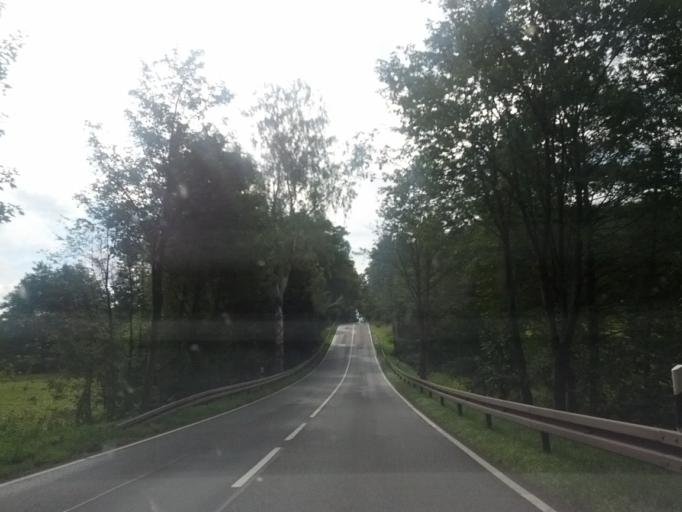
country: DE
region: Thuringia
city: Wolfsburg-Unkeroda
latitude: 50.8692
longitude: 10.2848
